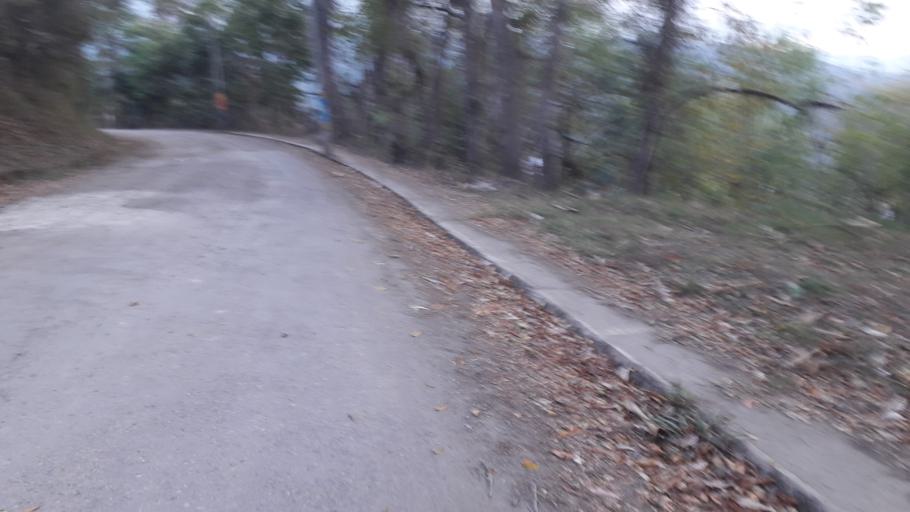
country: CO
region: Boyaca
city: Guayata
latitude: 4.9676
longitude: -73.4887
